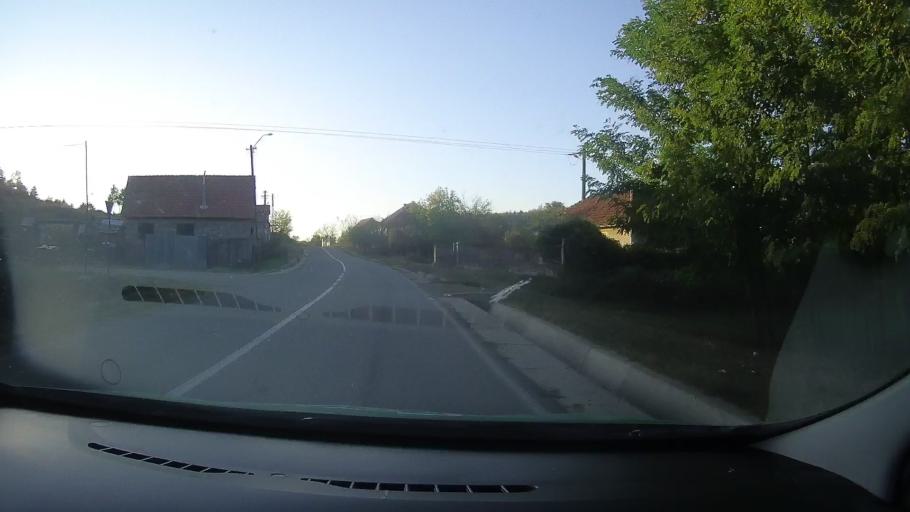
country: RO
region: Timis
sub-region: Comuna Traian Vuia
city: Traian Vuia
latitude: 45.7598
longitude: 22.1037
